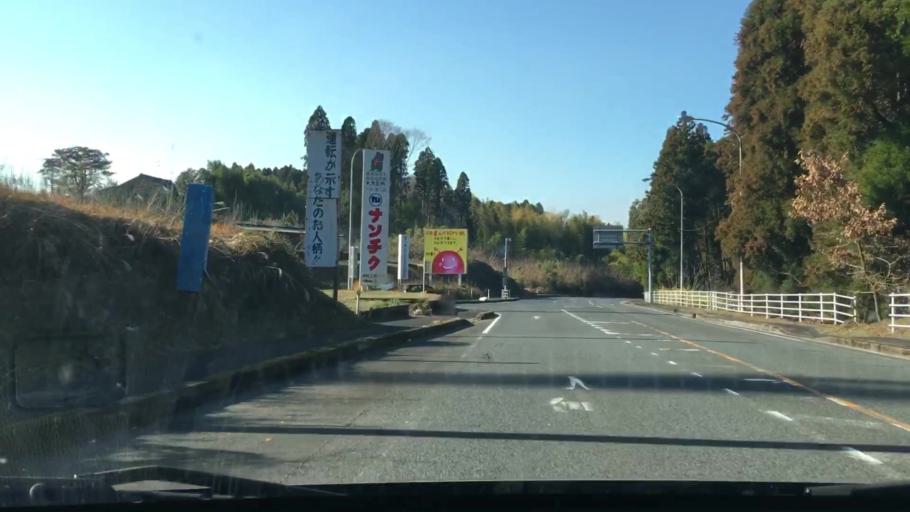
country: JP
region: Kagoshima
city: Sueyoshicho-ninokata
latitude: 31.6750
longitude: 130.9271
